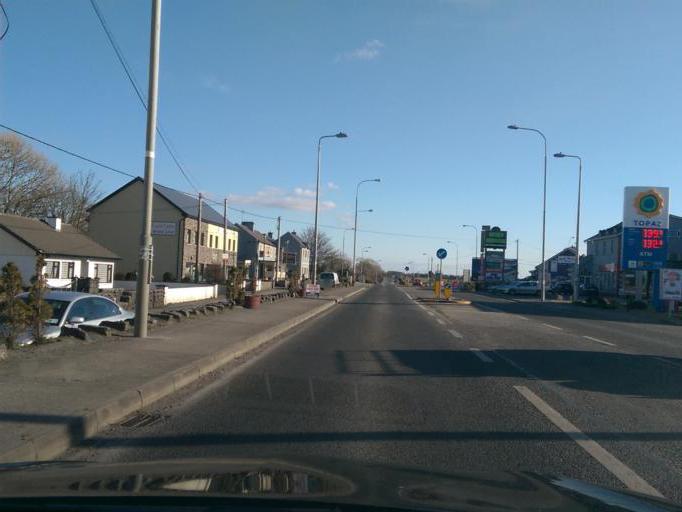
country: IE
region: Connaught
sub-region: County Galway
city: Oranmore
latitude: 53.2092
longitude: -8.8686
